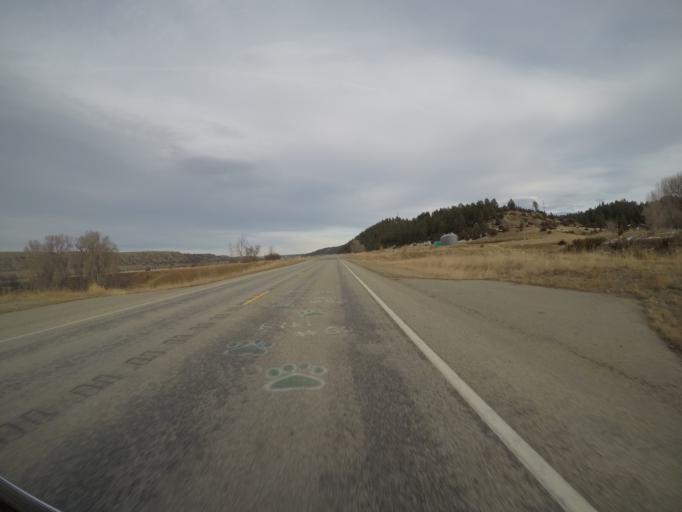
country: US
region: Montana
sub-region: Stillwater County
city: Absarokee
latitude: 45.5484
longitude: -109.3707
